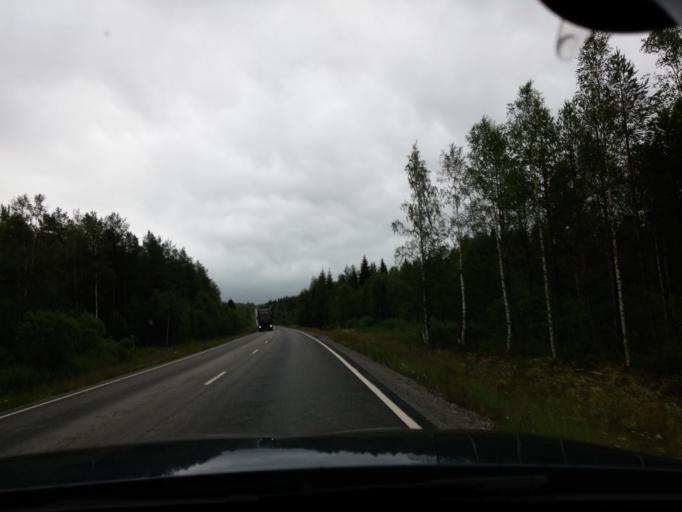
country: FI
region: Central Finland
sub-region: Saarijaervi-Viitasaari
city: Pylkoenmaeki
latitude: 62.6408
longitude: 24.8760
